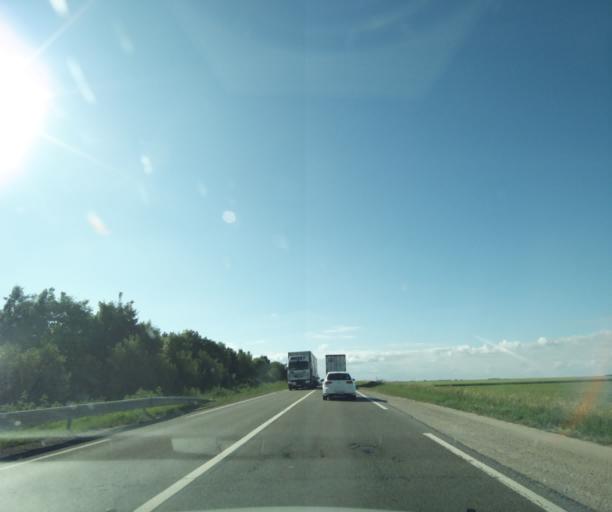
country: FR
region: Centre
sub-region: Departement d'Eure-et-Loir
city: Voves
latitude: 48.2758
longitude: 1.7384
